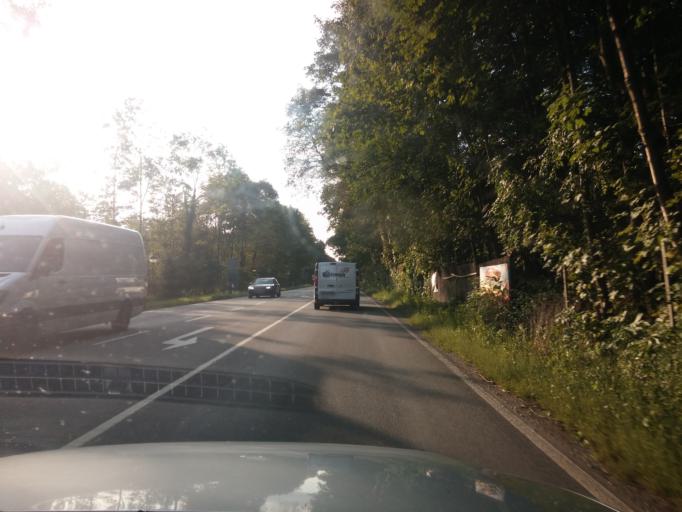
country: DE
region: Bavaria
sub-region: Upper Bavaria
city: Vaterstetten
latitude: 48.0922
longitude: 11.7830
